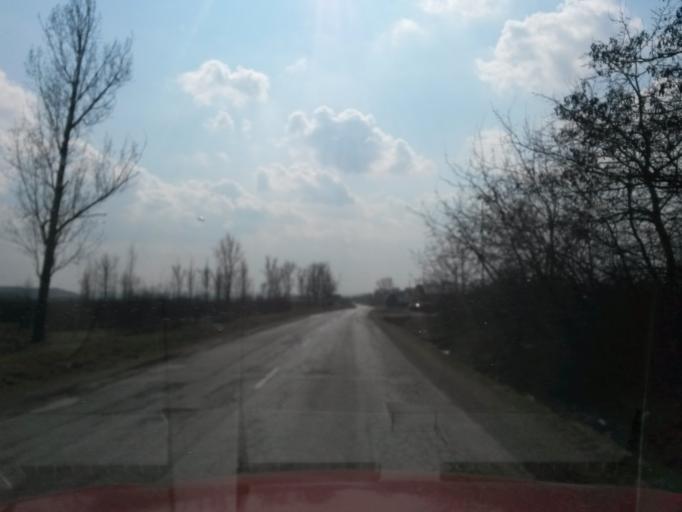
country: SK
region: Kosicky
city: Kosice
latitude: 48.6058
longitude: 21.1734
